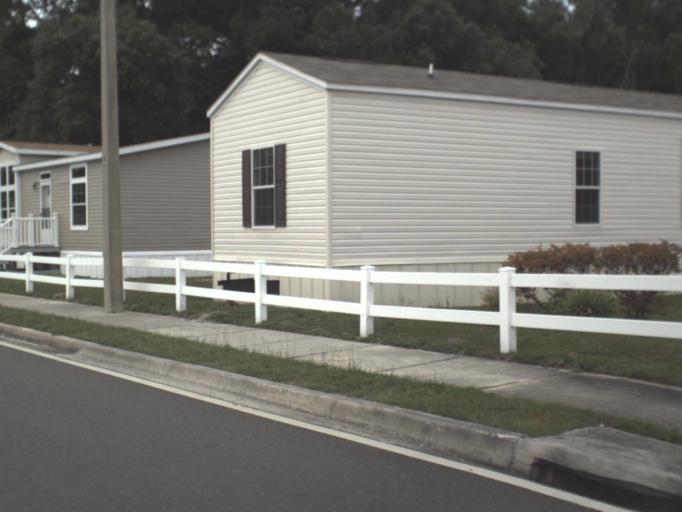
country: US
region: Florida
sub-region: Clay County
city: Bellair-Meadowbrook Terrace
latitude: 30.2397
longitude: -81.7413
